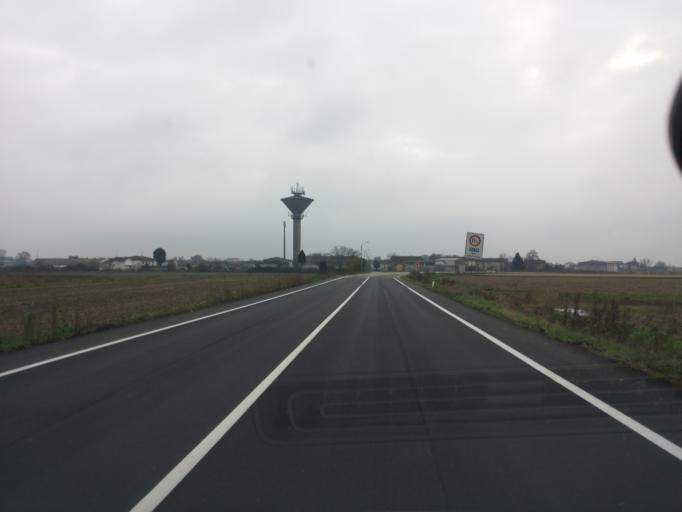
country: IT
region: Piedmont
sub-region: Provincia di Alessandria
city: Villanova Monferrato
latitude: 45.1890
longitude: 8.4727
